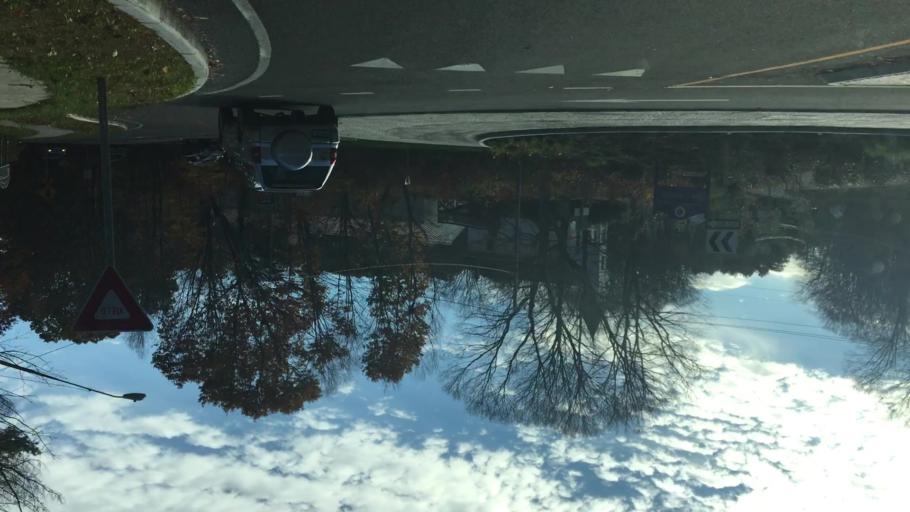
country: US
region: Connecticut
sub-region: New Haven County
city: Seymour
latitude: 41.3788
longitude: -73.1269
